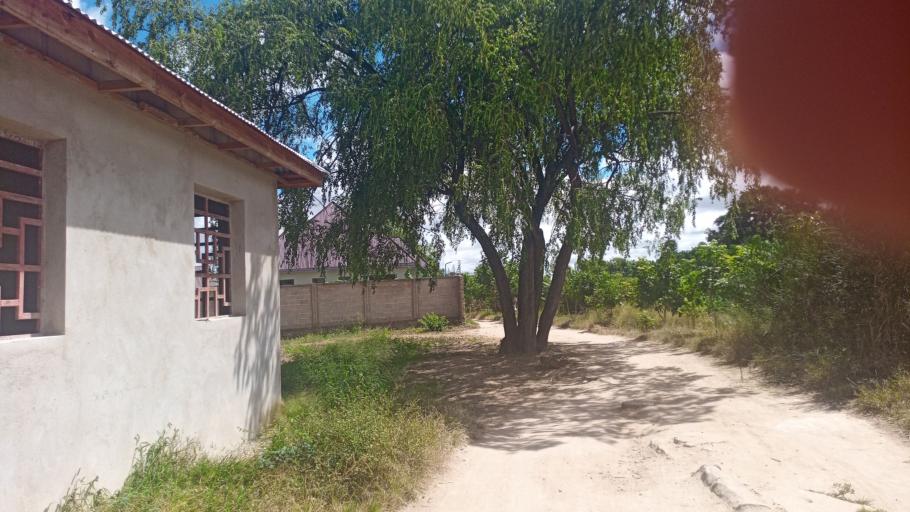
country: TZ
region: Dodoma
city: Dodoma
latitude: -6.1923
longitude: 35.7307
